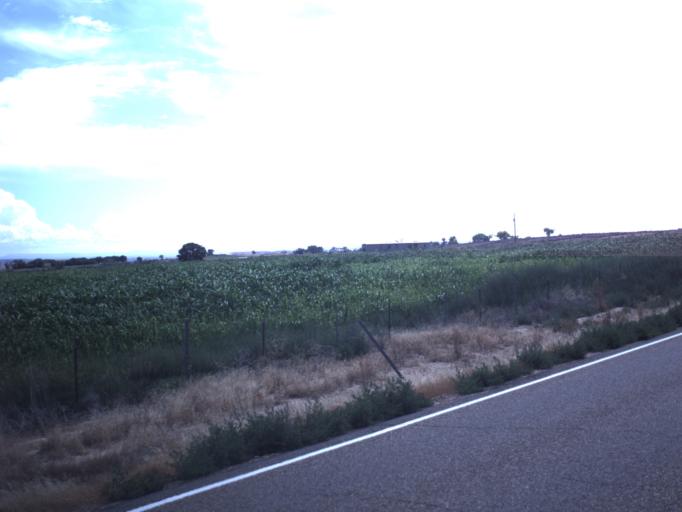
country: US
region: Utah
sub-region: Uintah County
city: Maeser
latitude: 40.2413
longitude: -109.6844
